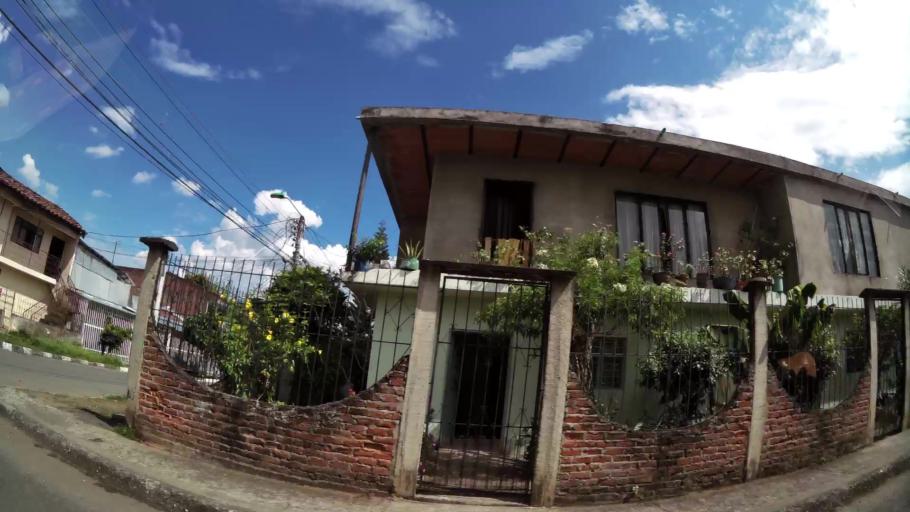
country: CO
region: Valle del Cauca
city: Cali
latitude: 3.4024
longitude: -76.5142
